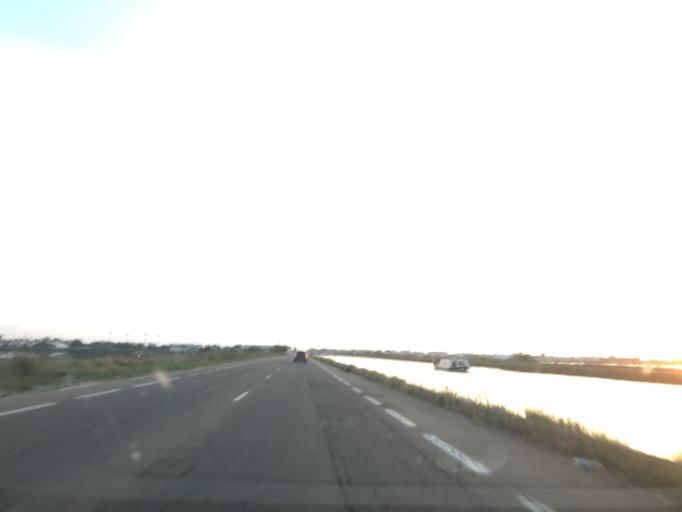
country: FR
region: Languedoc-Roussillon
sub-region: Departement du Gard
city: Le Grau-du-Roi
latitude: 43.5442
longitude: 4.1528
